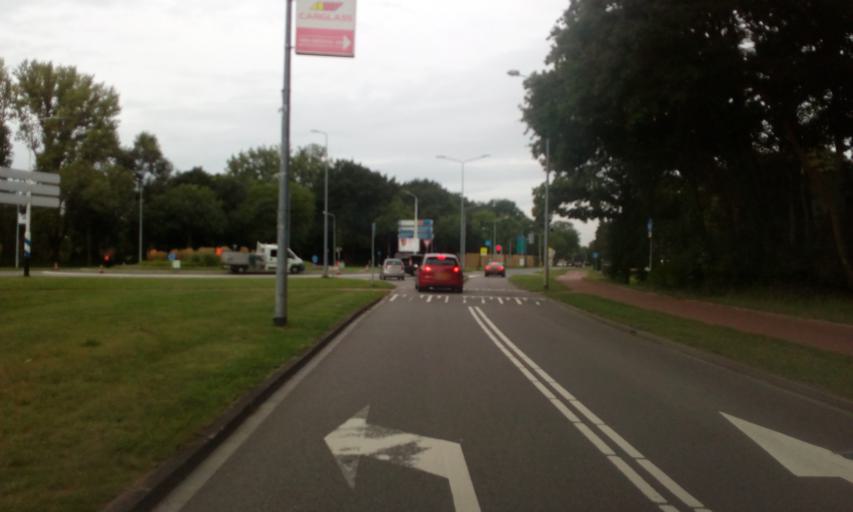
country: NL
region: North Holland
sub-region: Gemeente Wijdemeren
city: Nieuw-Loosdrecht
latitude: 52.2201
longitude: 5.1459
